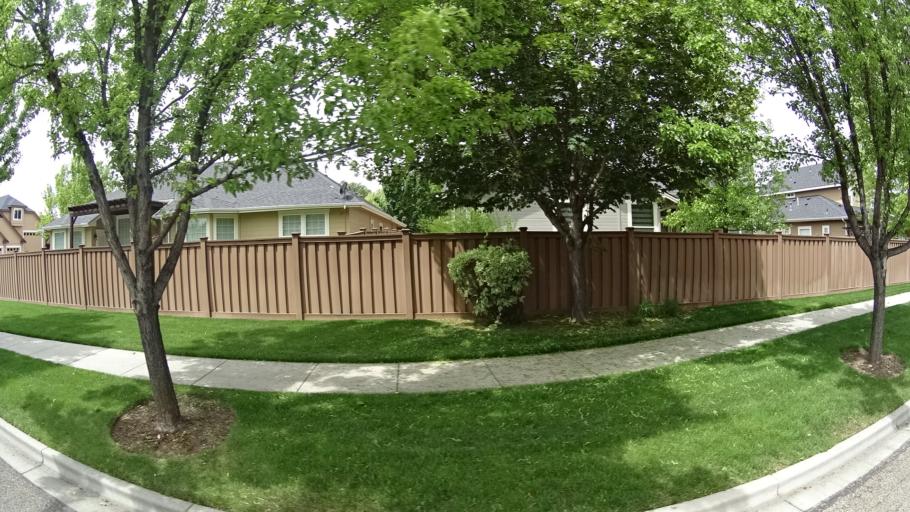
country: US
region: Idaho
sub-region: Ada County
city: Meridian
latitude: 43.5583
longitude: -116.3244
